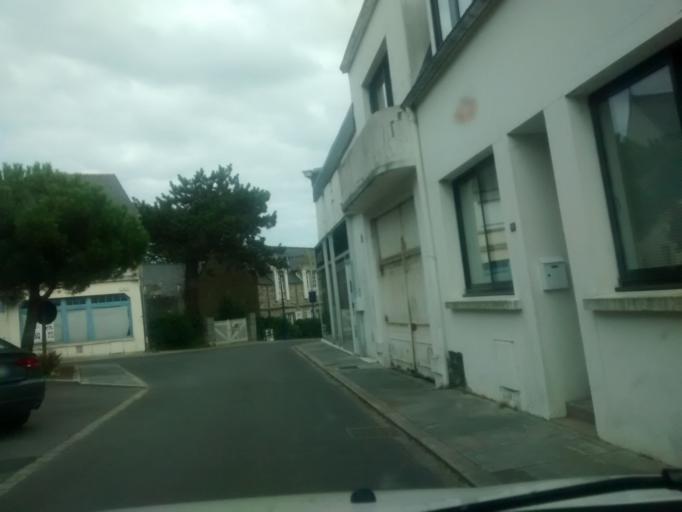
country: FR
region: Brittany
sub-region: Departement d'Ille-et-Vilaine
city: Saint-Lunaire
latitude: 48.6356
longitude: -2.1102
